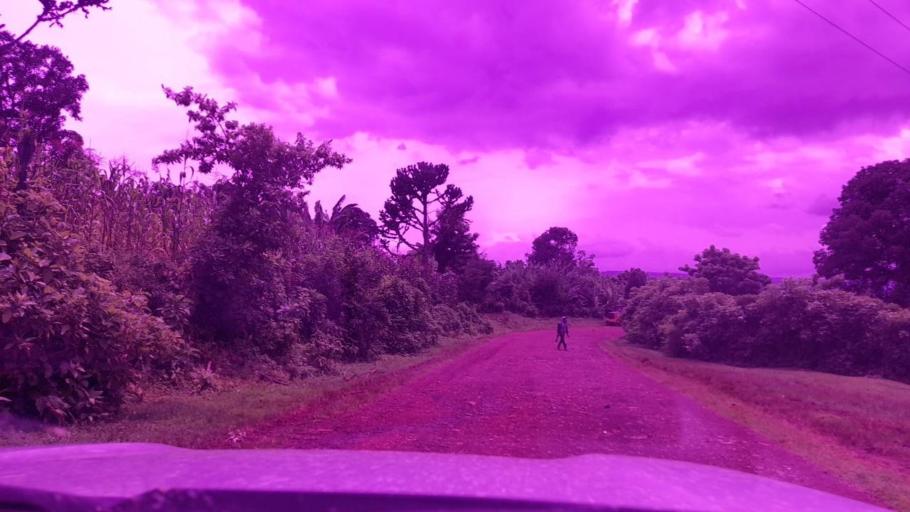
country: ET
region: Southern Nations, Nationalities, and People's Region
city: Tippi
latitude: 7.6271
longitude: 35.5811
